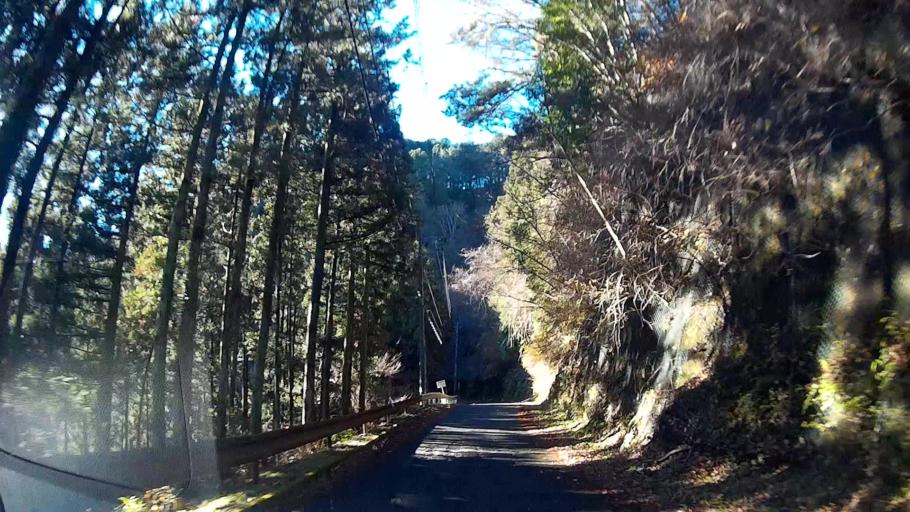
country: JP
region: Saitama
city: Chichibu
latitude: 35.9465
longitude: 139.1777
